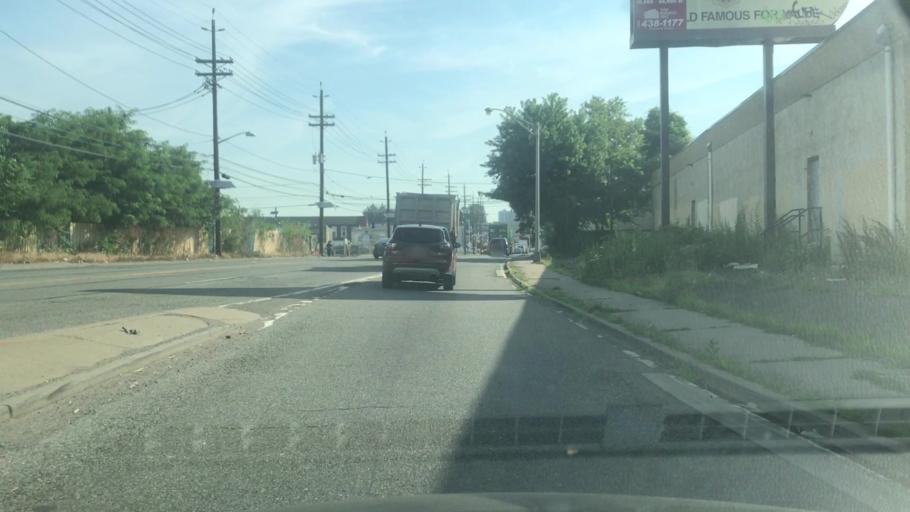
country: US
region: New Jersey
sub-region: Hudson County
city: Union City
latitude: 40.7807
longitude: -74.0368
